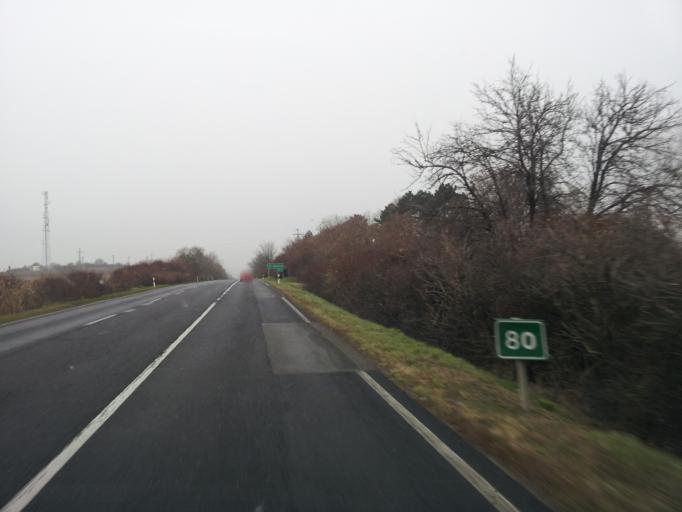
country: HU
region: Veszprem
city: Ajka
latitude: 47.1397
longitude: 17.5889
